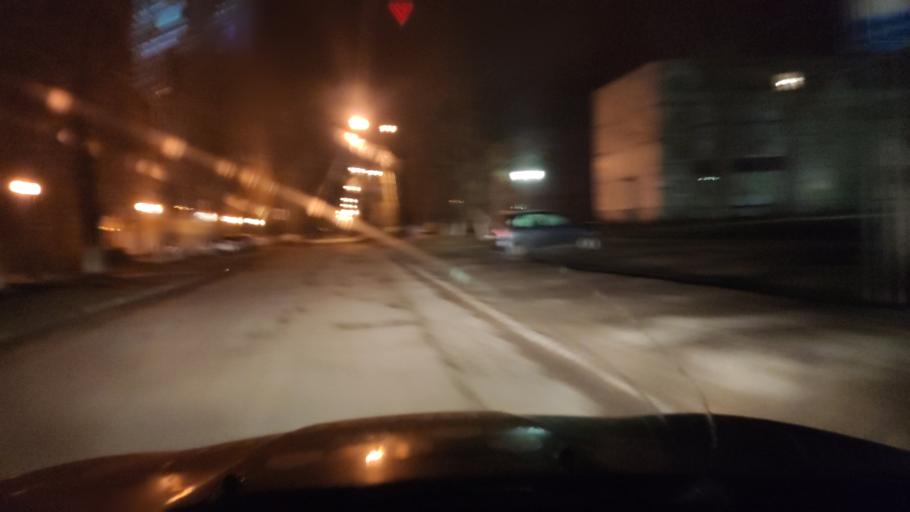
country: RU
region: Samara
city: Povolzhskiy
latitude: 53.5857
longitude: 49.7614
